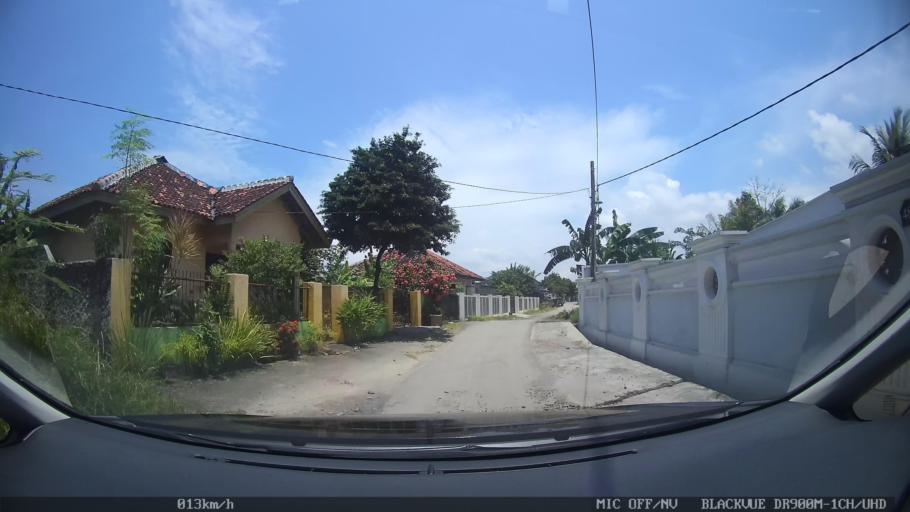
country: ID
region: Lampung
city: Kedaton
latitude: -5.3730
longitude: 105.2853
